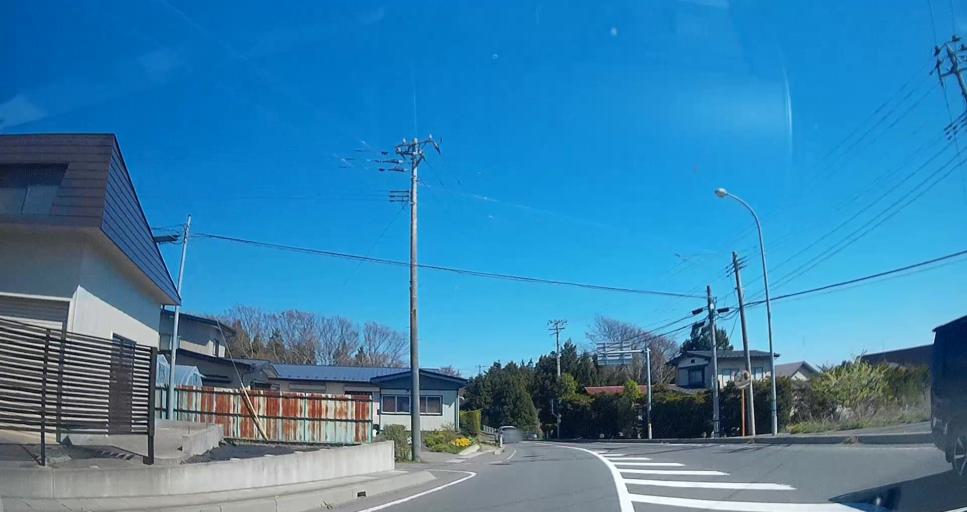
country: JP
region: Aomori
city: Misawa
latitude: 40.6369
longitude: 141.4428
